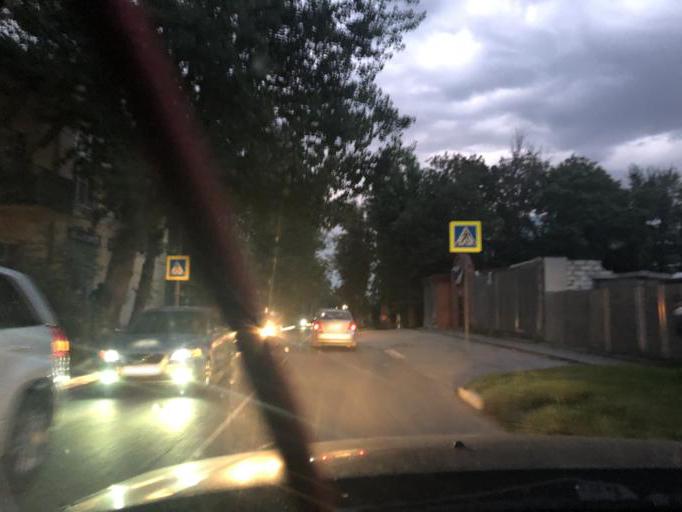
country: RU
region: Tula
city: Tula
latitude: 54.2263
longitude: 37.6197
